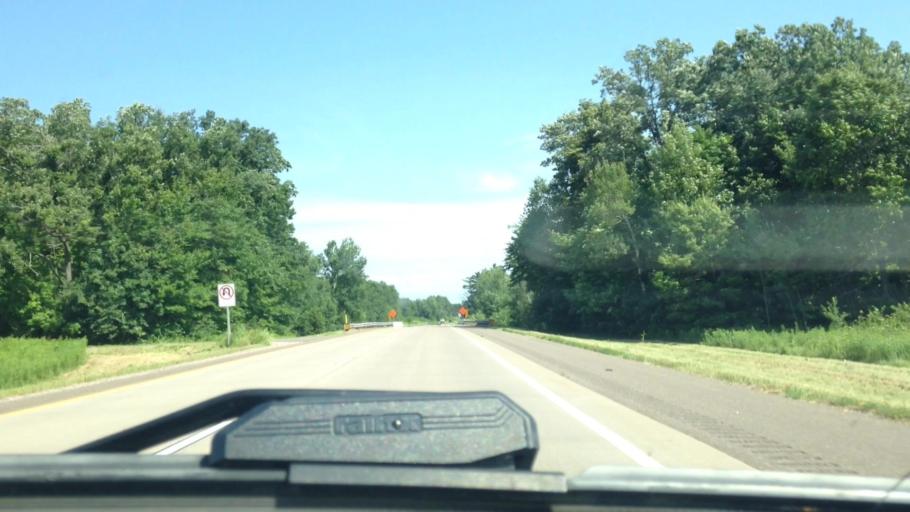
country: US
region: Wisconsin
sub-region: Barron County
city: Rice Lake
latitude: 45.5520
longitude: -91.7642
